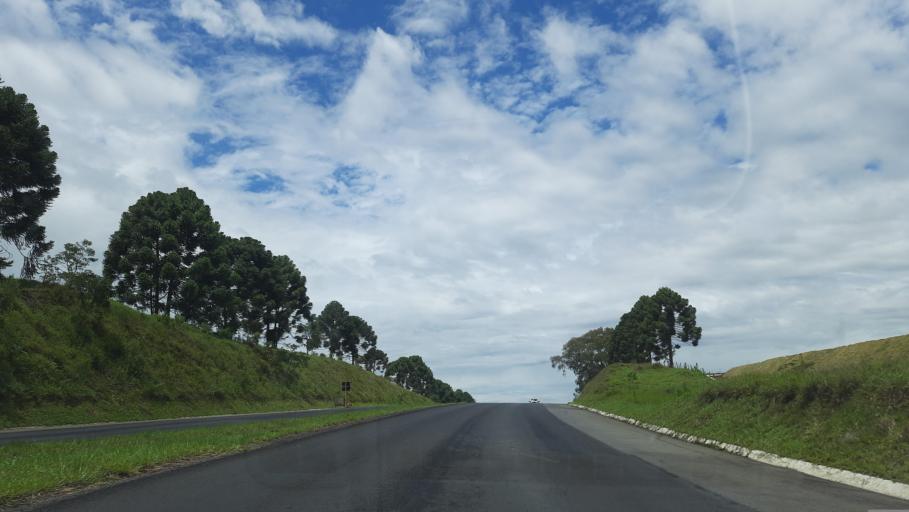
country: BR
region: Minas Gerais
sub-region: Pocos De Caldas
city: Pocos de Caldas
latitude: -21.8243
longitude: -46.6706
